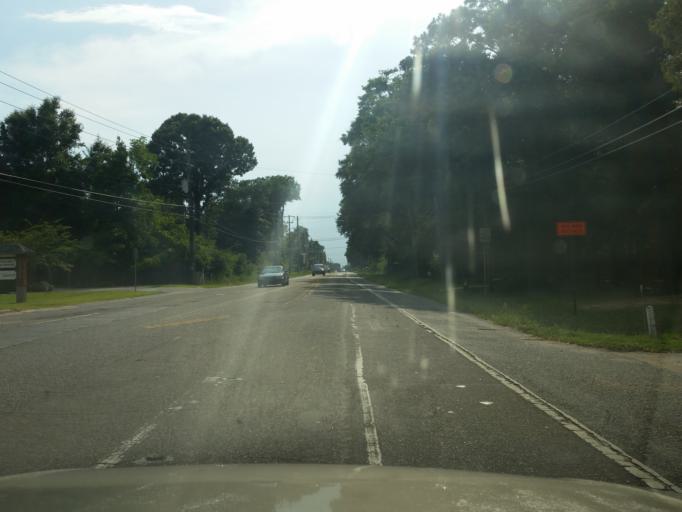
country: US
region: Florida
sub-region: Escambia County
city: Ferry Pass
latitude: 30.5100
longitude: -87.1993
